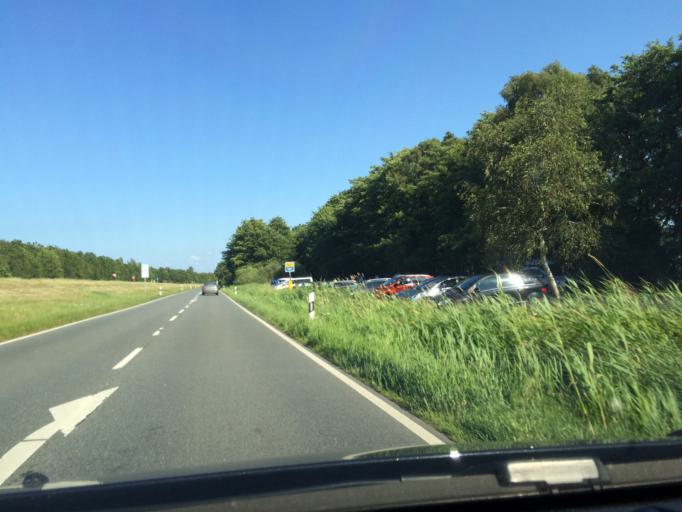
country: DE
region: Mecklenburg-Vorpommern
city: Ostseebad Prerow
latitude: 54.4473
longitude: 12.6179
